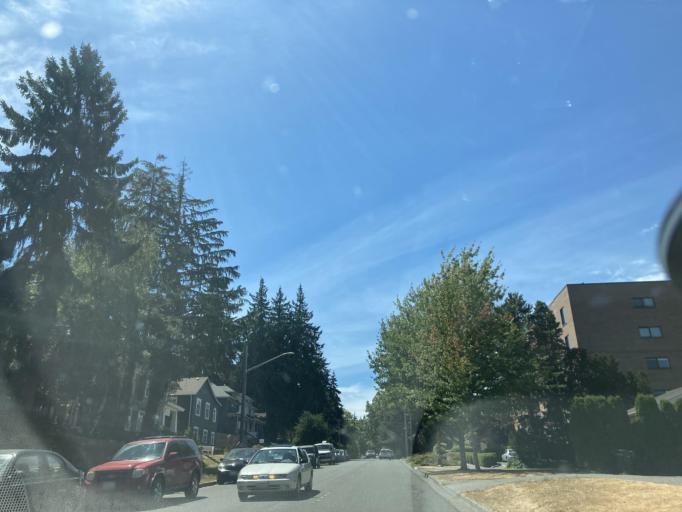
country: US
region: Washington
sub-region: Whatcom County
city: Bellingham
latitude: 48.7418
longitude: -122.4829
